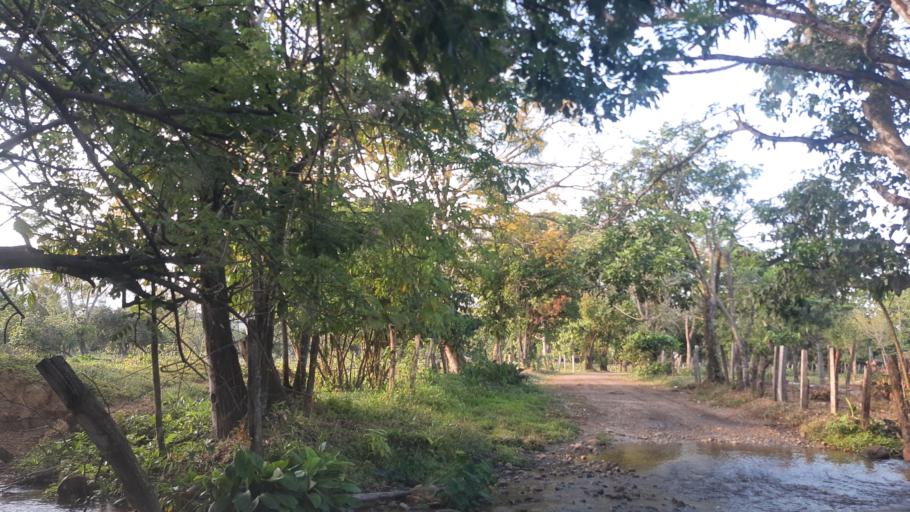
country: CO
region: Arauca
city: Tame
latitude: 6.4976
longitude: -71.7676
